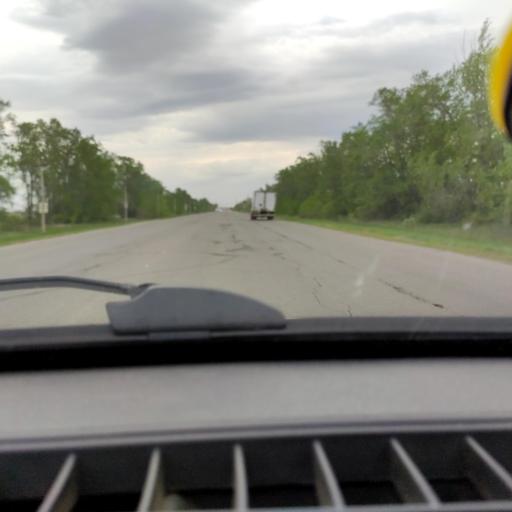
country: RU
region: Samara
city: Tol'yatti
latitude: 53.5926
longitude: 49.4069
